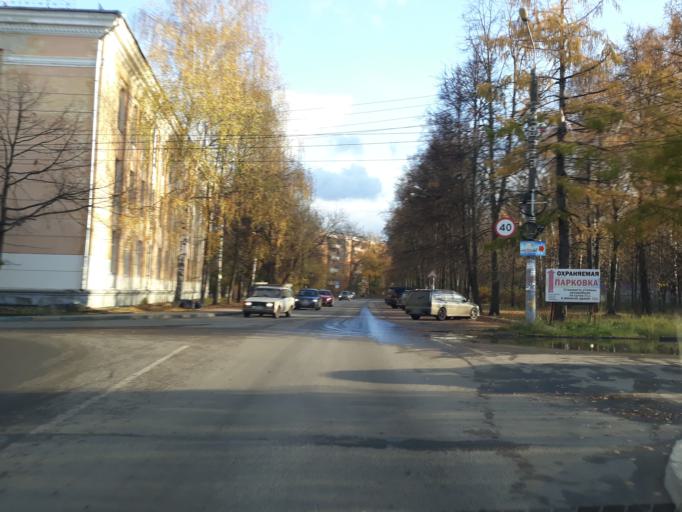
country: RU
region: Nizjnij Novgorod
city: Neklyudovo
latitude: 56.3433
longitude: 43.8645
